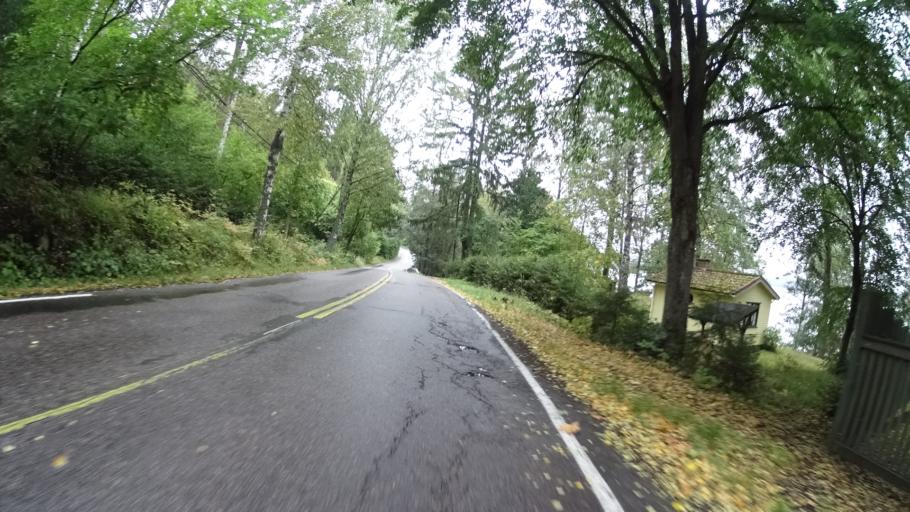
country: FI
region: Uusimaa
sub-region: Helsinki
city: Espoo
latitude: 60.2630
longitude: 24.6544
